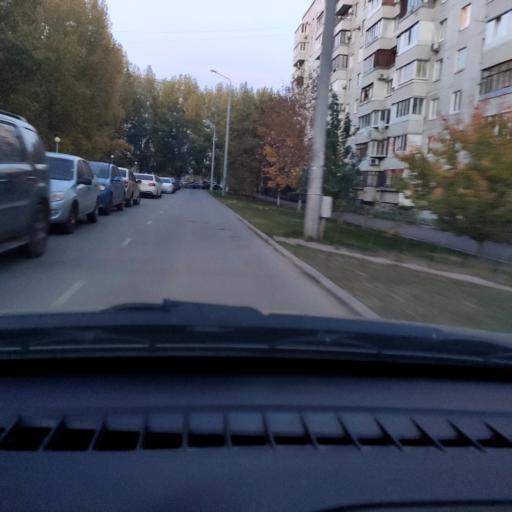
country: RU
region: Samara
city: Tol'yatti
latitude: 53.5464
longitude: 49.3367
